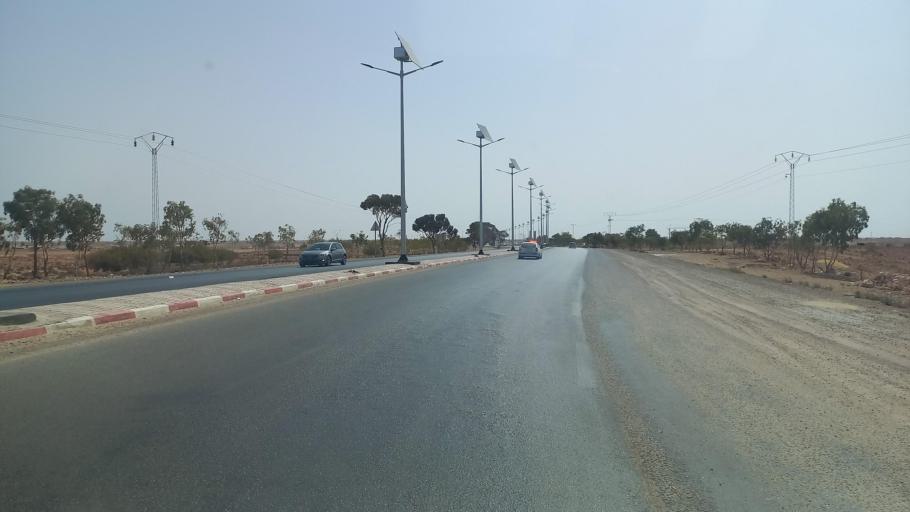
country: TN
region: Madanin
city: Medenine
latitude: 33.3603
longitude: 10.5617
